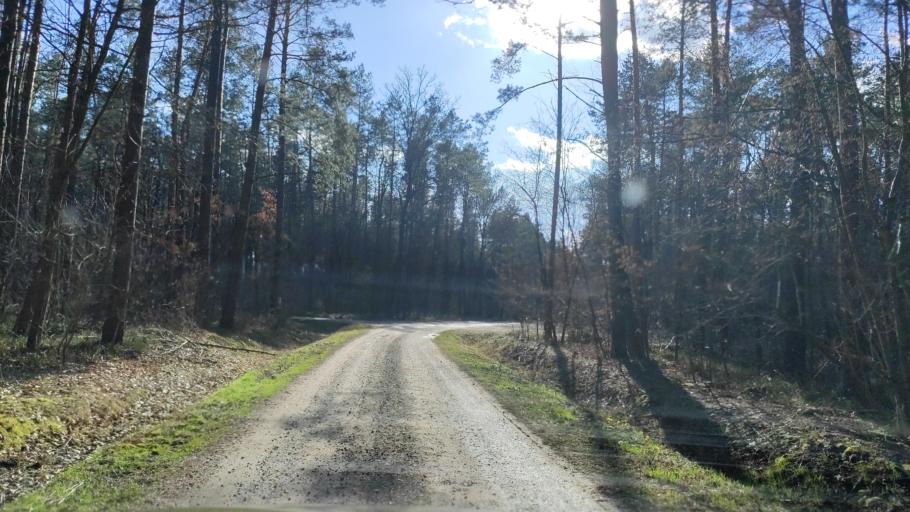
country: PL
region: Masovian Voivodeship
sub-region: Powiat radomski
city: Jastrzebia
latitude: 51.4708
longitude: 21.2425
